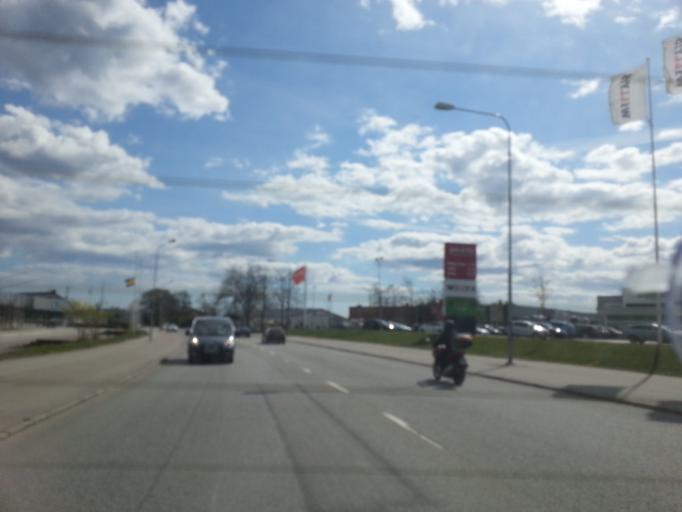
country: SE
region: Skane
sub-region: Ystads Kommun
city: Ystad
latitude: 55.4391
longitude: 13.8353
